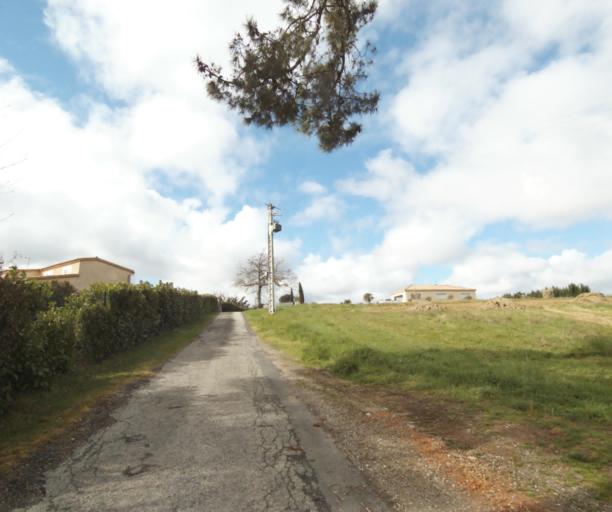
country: FR
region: Midi-Pyrenees
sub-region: Departement de l'Ariege
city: Saverdun
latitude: 43.2145
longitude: 1.5660
